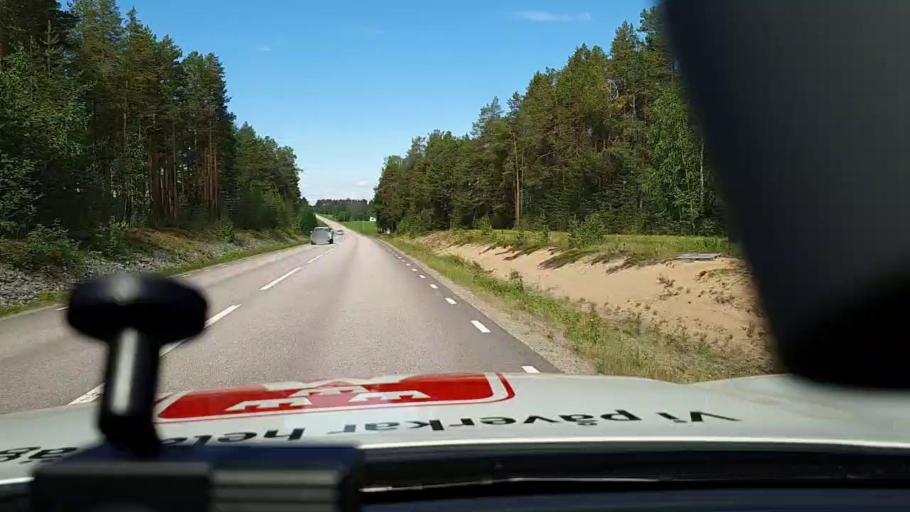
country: SE
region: Norrbotten
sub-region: Lulea Kommun
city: Sodra Sunderbyn
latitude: 65.6358
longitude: 21.9168
